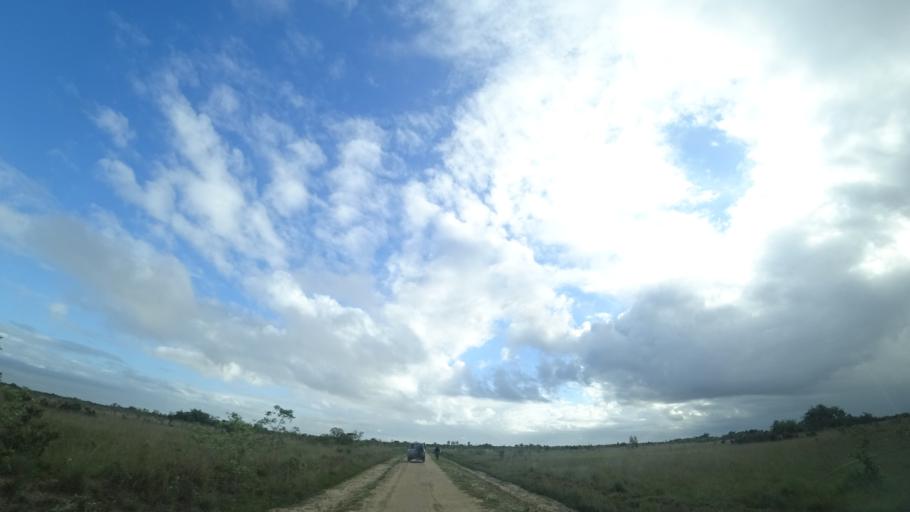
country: MZ
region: Sofala
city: Beira
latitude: -19.6758
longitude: 35.0593
